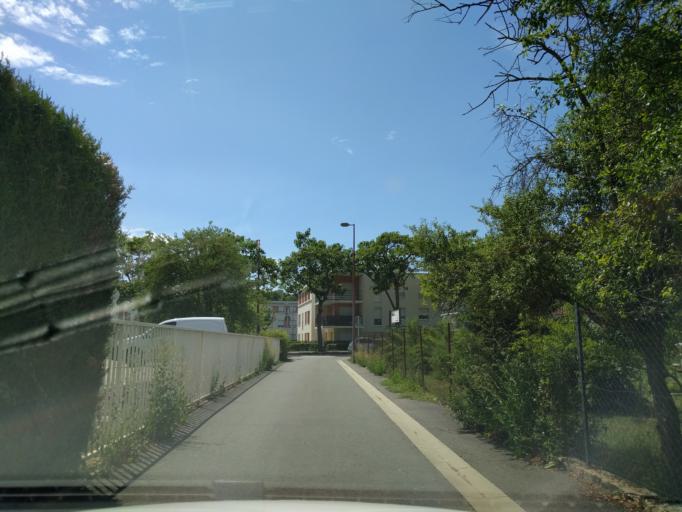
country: FR
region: Lorraine
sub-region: Departement de la Moselle
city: Woippy
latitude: 49.1383
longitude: 6.1493
